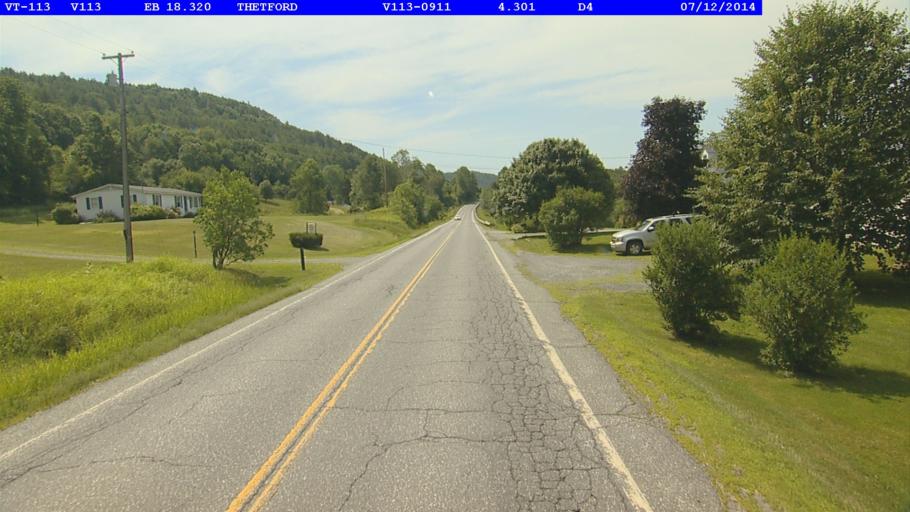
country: US
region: New Hampshire
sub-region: Grafton County
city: Lyme
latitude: 43.8395
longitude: -72.2471
